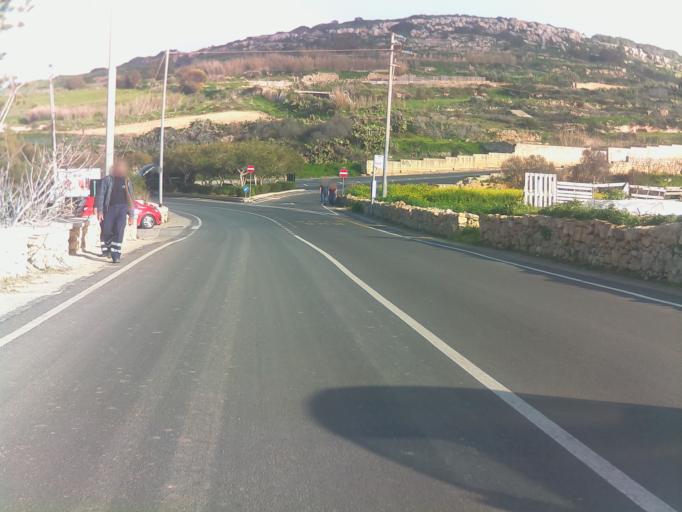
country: MT
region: L-Imgarr
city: Imgarr
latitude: 35.9307
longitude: 14.3487
